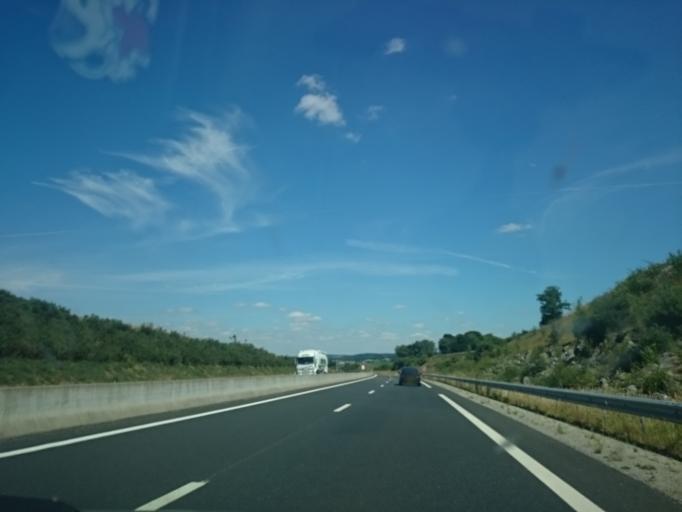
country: FR
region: Brittany
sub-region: Departement des Cotes-d'Armor
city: Gouarec
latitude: 48.2331
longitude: -3.2055
